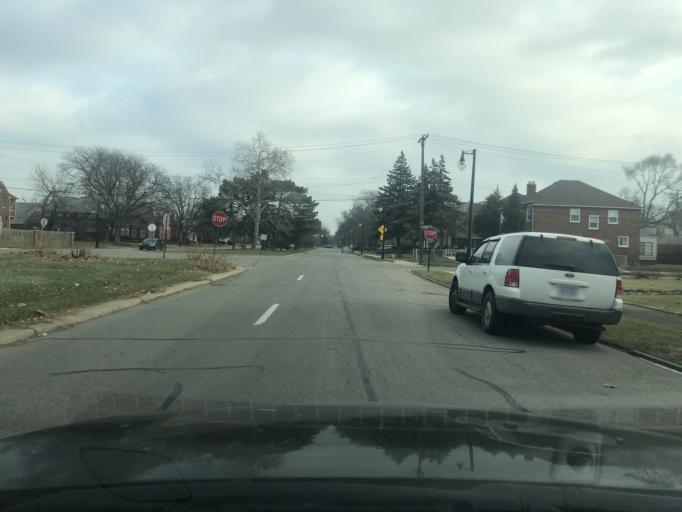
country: US
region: Michigan
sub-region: Wayne County
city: Highland Park
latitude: 42.3917
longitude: -83.1359
